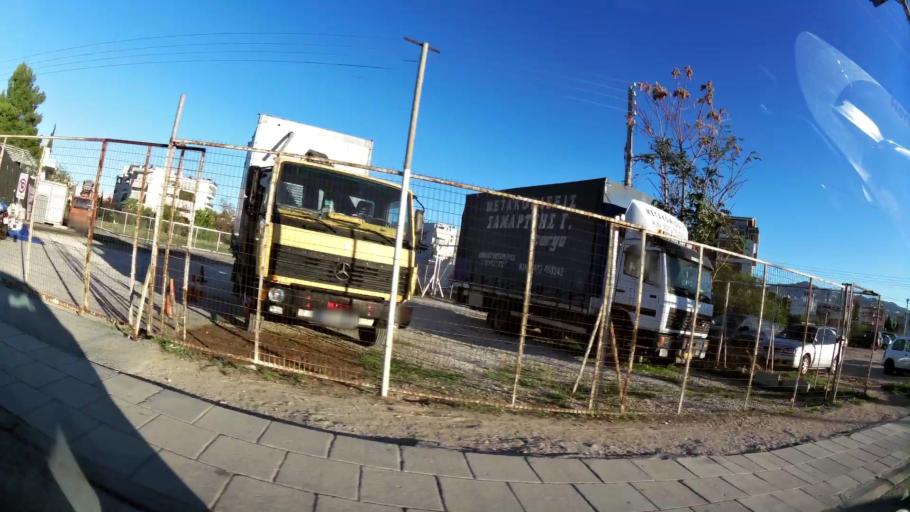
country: GR
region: Attica
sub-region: Nomarchia Athinas
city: Agia Paraskevi
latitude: 38.0223
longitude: 23.8236
